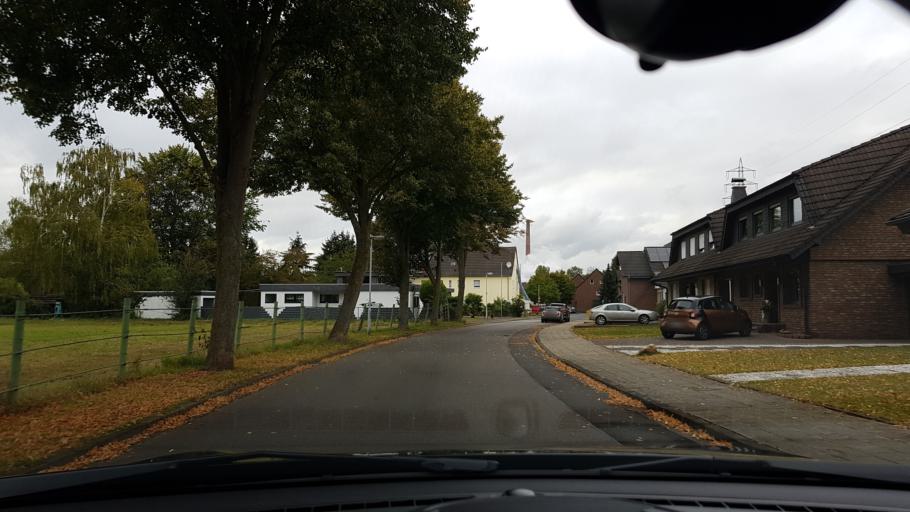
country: DE
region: North Rhine-Westphalia
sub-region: Regierungsbezirk Koln
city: Bergheim
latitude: 50.9804
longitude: 6.6630
